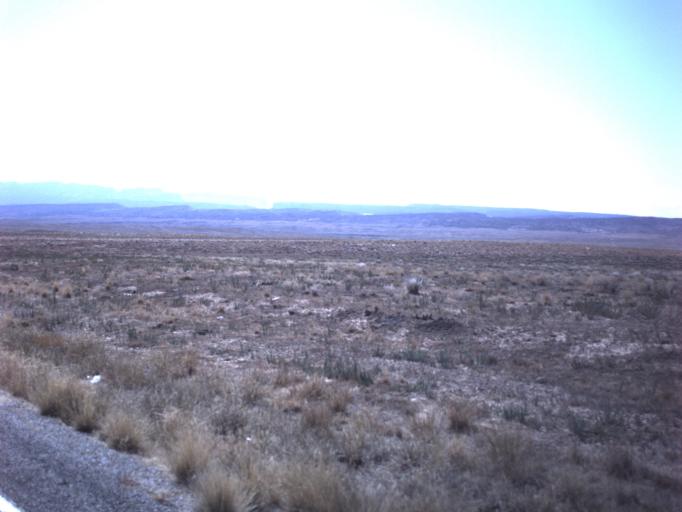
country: US
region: Utah
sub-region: Grand County
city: Moab
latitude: 38.9285
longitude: -109.3418
